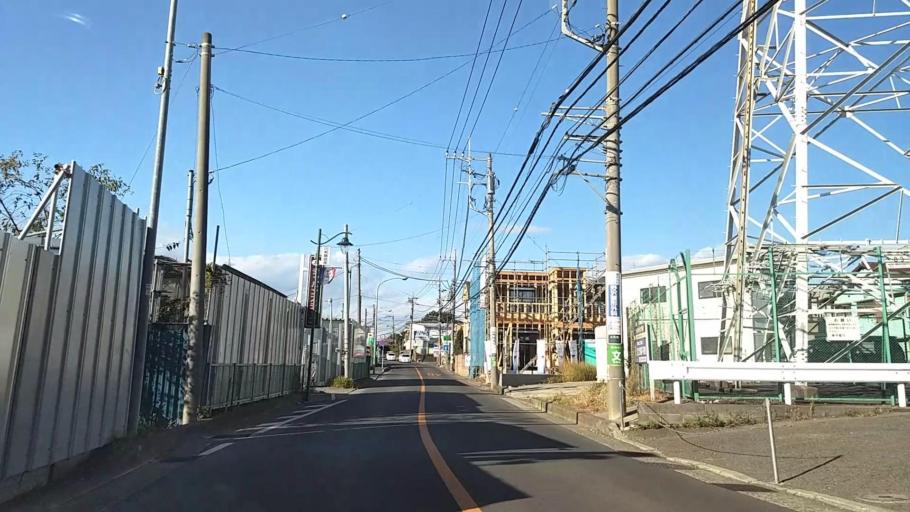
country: JP
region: Tokyo
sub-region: Machida-shi
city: Machida
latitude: 35.5334
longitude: 139.5463
